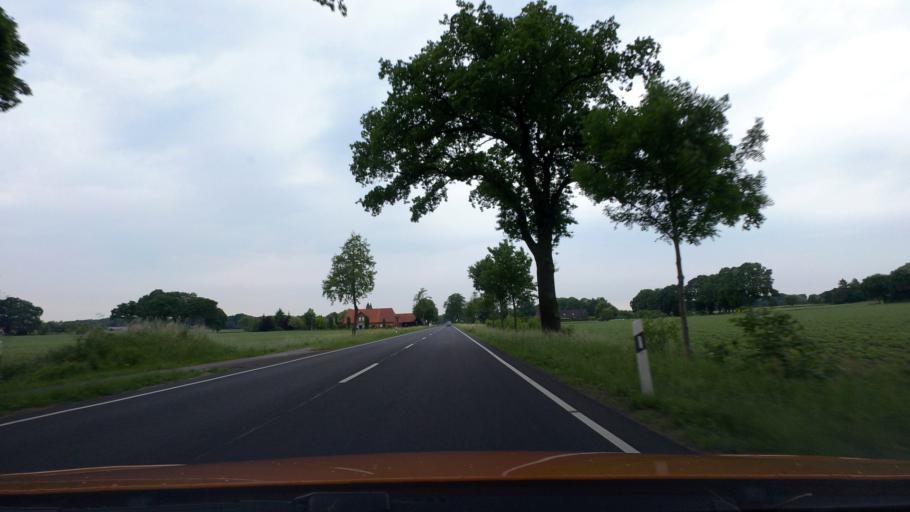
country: DE
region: Lower Saxony
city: Wietzen
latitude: 52.6967
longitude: 9.0873
